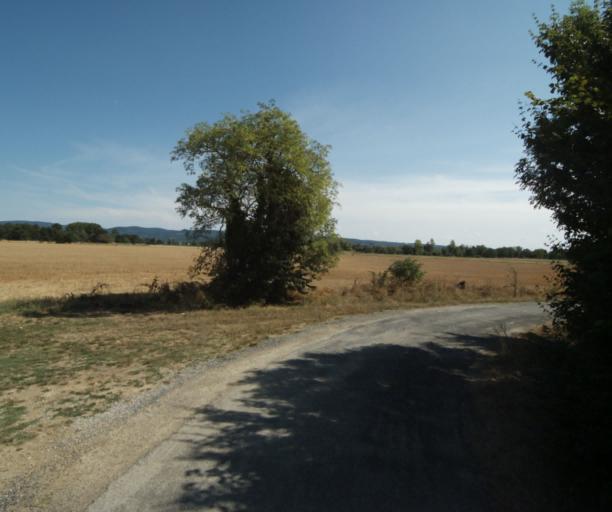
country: FR
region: Midi-Pyrenees
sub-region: Departement de la Haute-Garonne
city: Revel
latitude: 43.4844
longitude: 1.9764
